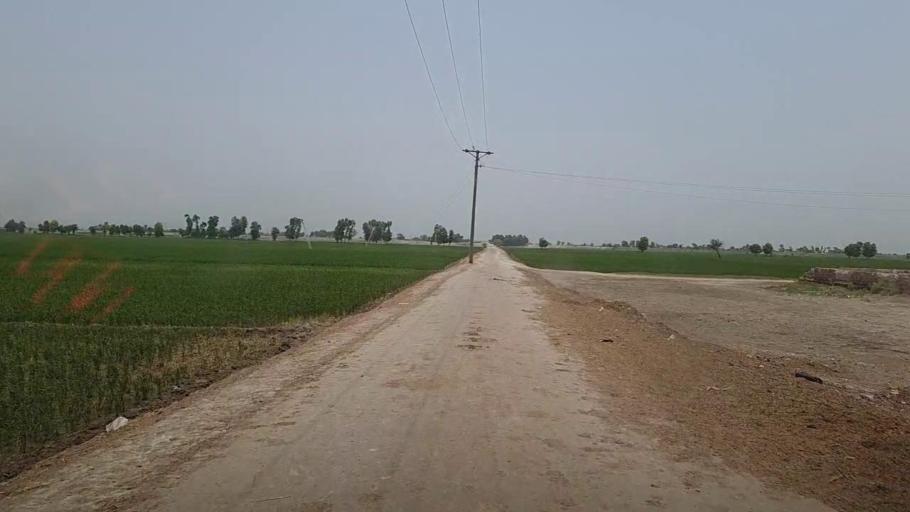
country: PK
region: Sindh
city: Sita Road
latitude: 27.0442
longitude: 67.8466
